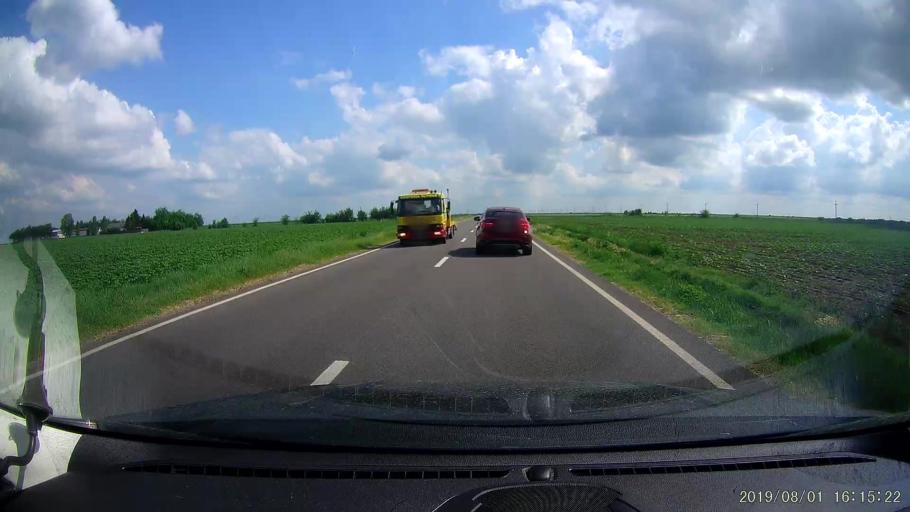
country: RO
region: Calarasi
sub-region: Comuna Stefan Voda
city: Stefan Voda
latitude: 44.3390
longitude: 27.3613
